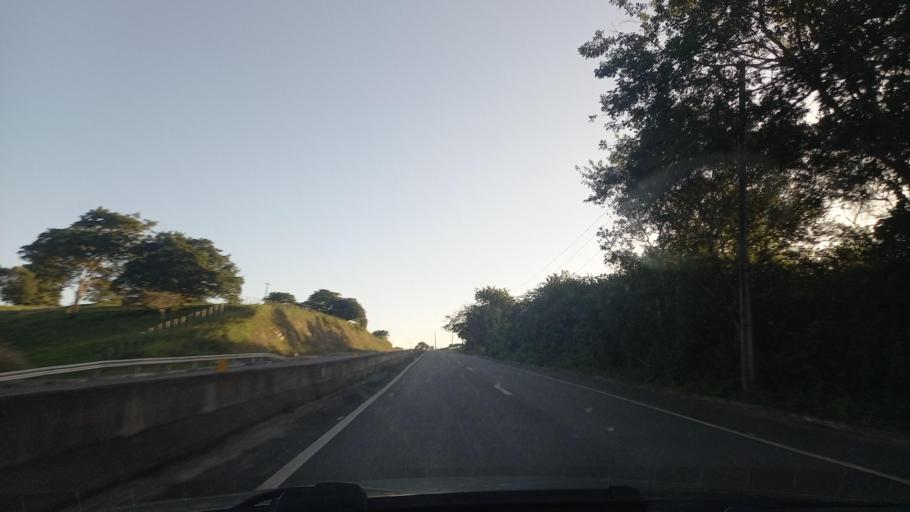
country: BR
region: Alagoas
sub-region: Limoeiro De Anadia
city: Limoeiro de Anadia
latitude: -9.7413
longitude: -36.4966
